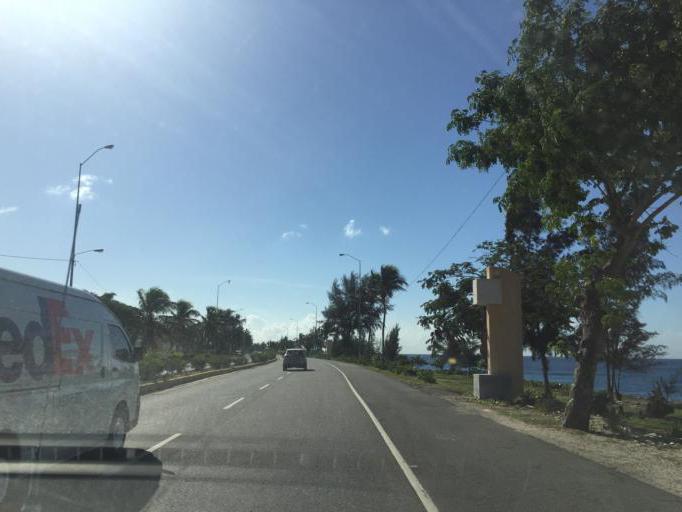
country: DO
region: Santo Domingo
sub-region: Santo Domingo
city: Boca Chica
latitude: 18.4383
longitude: -69.6815
